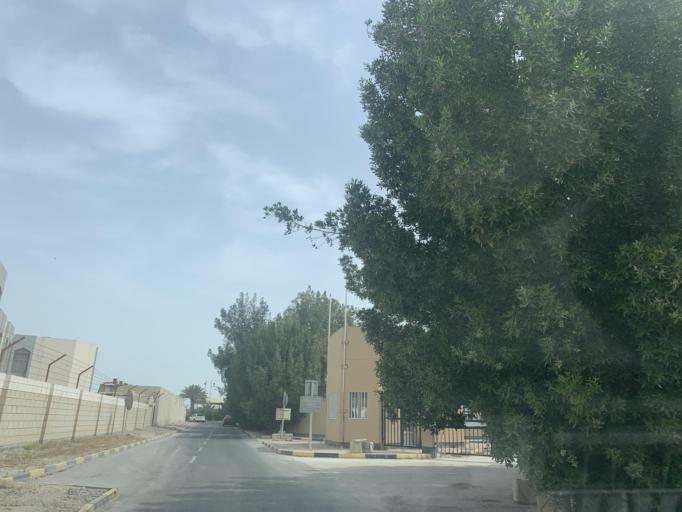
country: BH
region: Northern
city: Madinat `Isa
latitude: 26.1586
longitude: 50.5447
